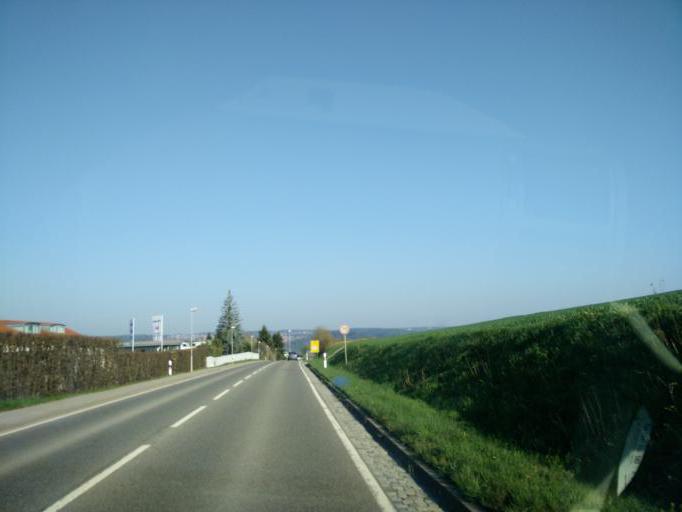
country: DE
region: Baden-Wuerttemberg
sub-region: Karlsruhe Region
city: Calw
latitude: 48.6991
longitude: 8.7633
